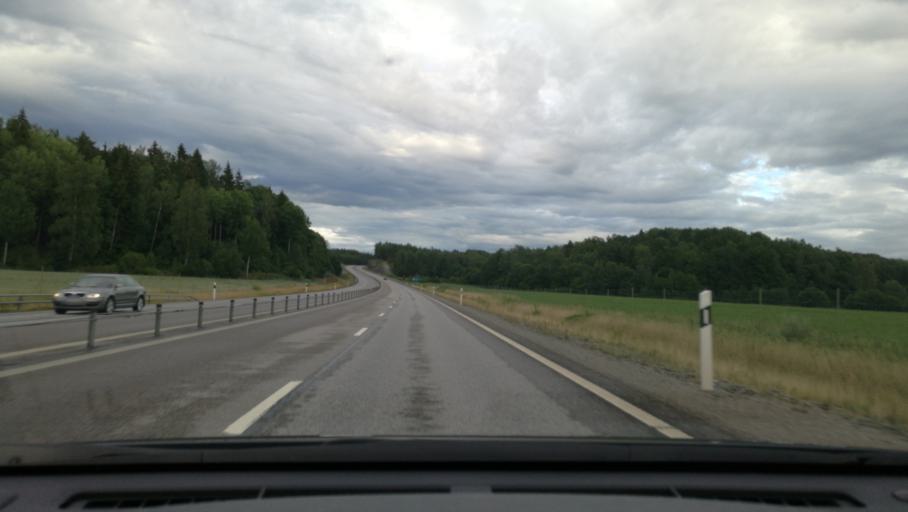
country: SE
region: OEstergoetland
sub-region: Norrkopings Kommun
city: Svartinge
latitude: 58.6710
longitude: 15.9721
